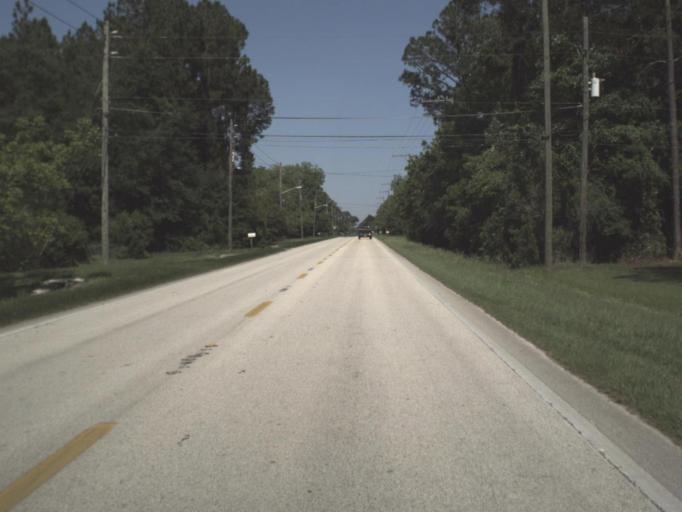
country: US
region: Florida
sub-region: Duval County
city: Baldwin
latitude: 30.3028
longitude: -82.0138
